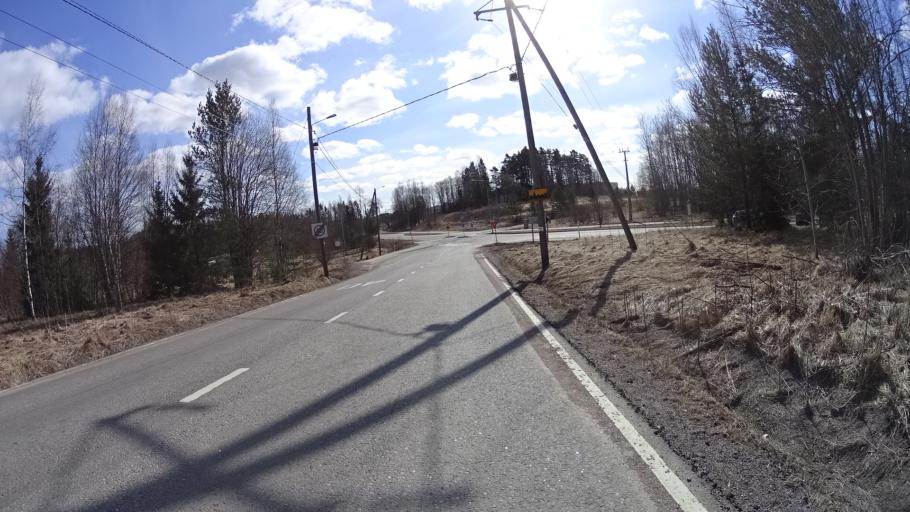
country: FI
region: Uusimaa
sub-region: Helsinki
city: Kauniainen
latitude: 60.2667
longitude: 24.7344
